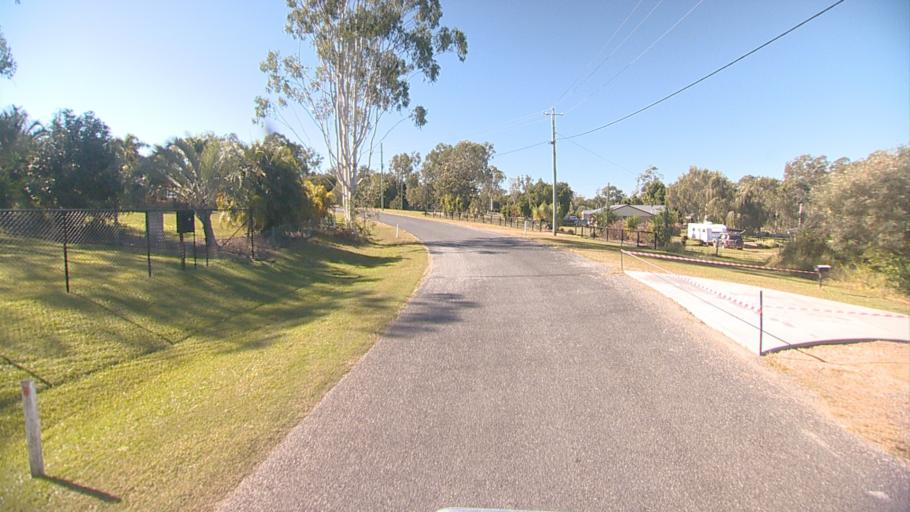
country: AU
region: Queensland
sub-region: Logan
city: Park Ridge South
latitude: -27.7340
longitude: 153.0410
